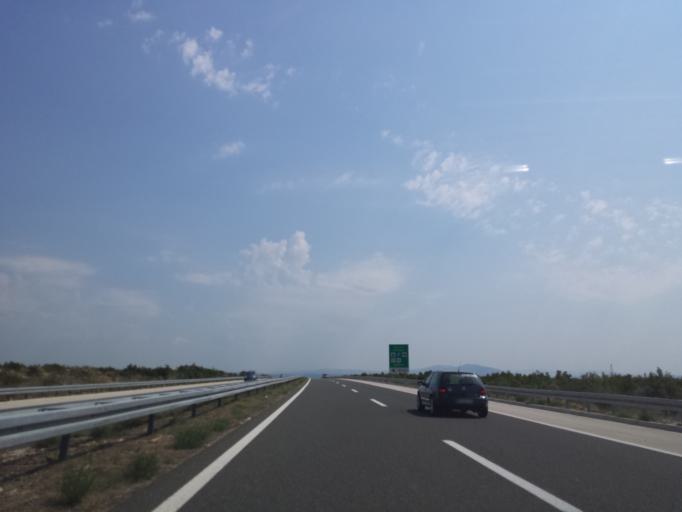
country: HR
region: Sibensko-Kniniska
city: Zaton
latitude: 43.8635
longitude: 15.8203
